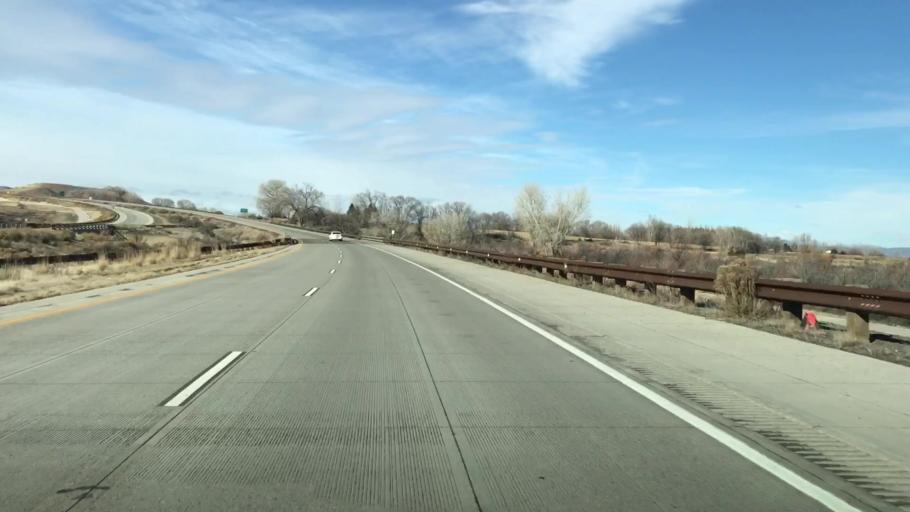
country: US
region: Colorado
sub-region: Mesa County
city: Loma
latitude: 39.1751
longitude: -108.7994
